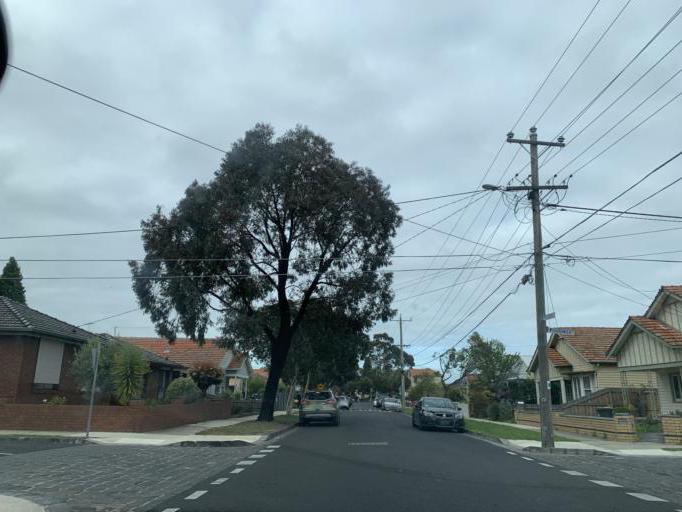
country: AU
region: Victoria
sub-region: Moreland
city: Coburg
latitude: -37.7494
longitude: 144.9705
